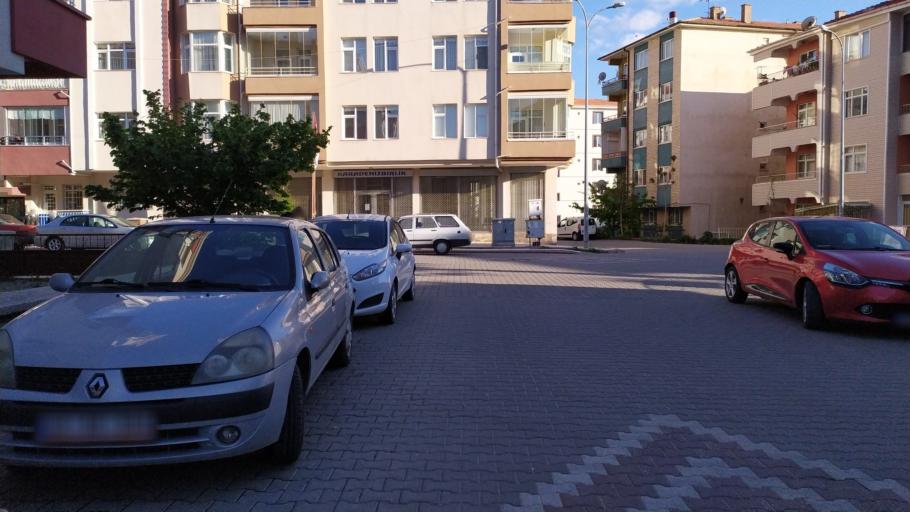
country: TR
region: Kirsehir
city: Kirsehir
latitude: 39.1519
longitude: 34.1586
